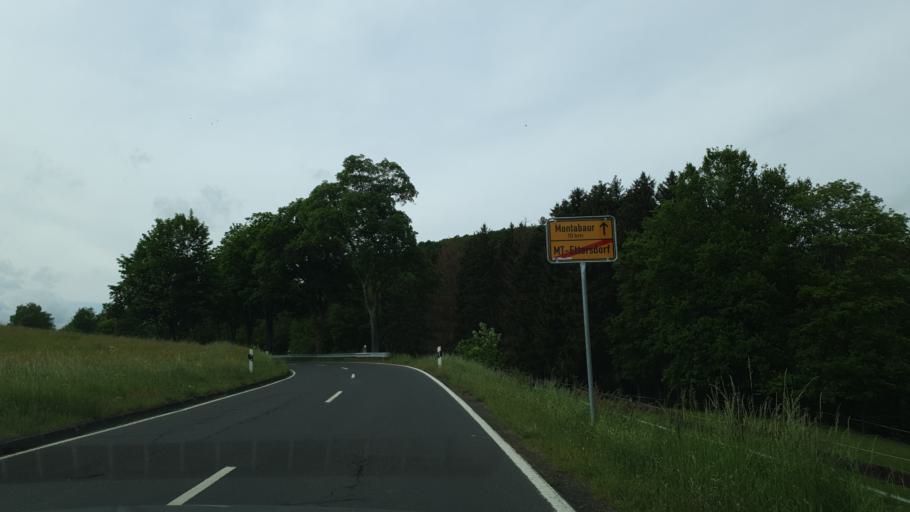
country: DE
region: Rheinland-Pfalz
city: Stahlhofen
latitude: 50.3973
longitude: 7.8795
